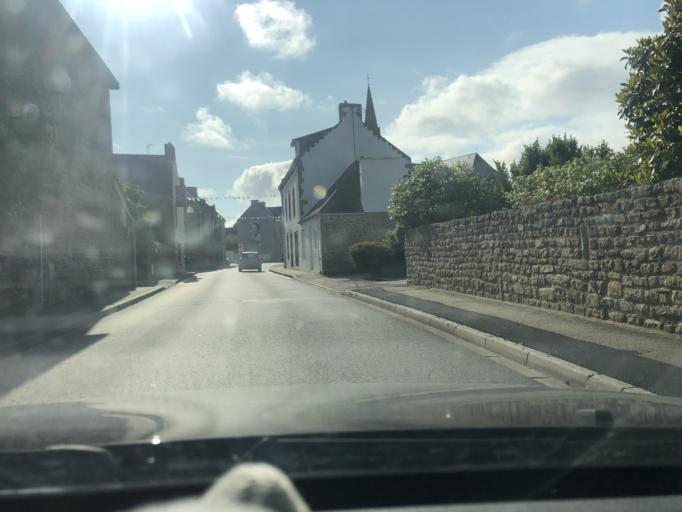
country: FR
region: Brittany
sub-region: Departement du Morbihan
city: Merlevenez
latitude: 47.6967
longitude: -3.2494
